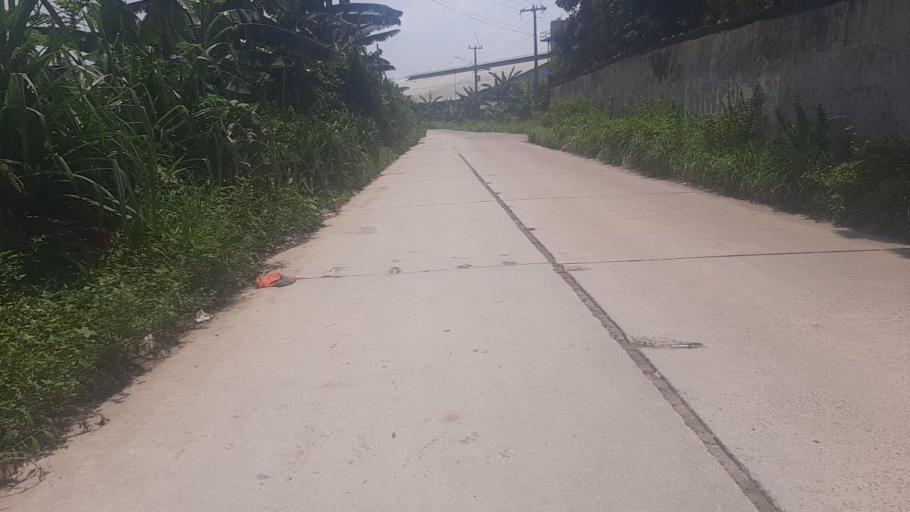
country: ID
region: West Java
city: Citeureup
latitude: -6.4611
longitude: 106.9298
